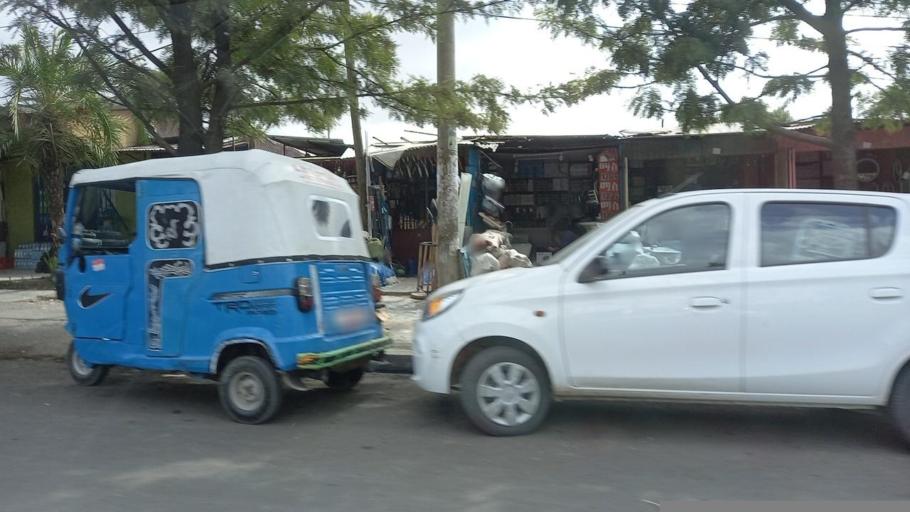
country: ET
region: Adis Abeba
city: Addis Ababa
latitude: 9.0205
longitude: 38.8578
